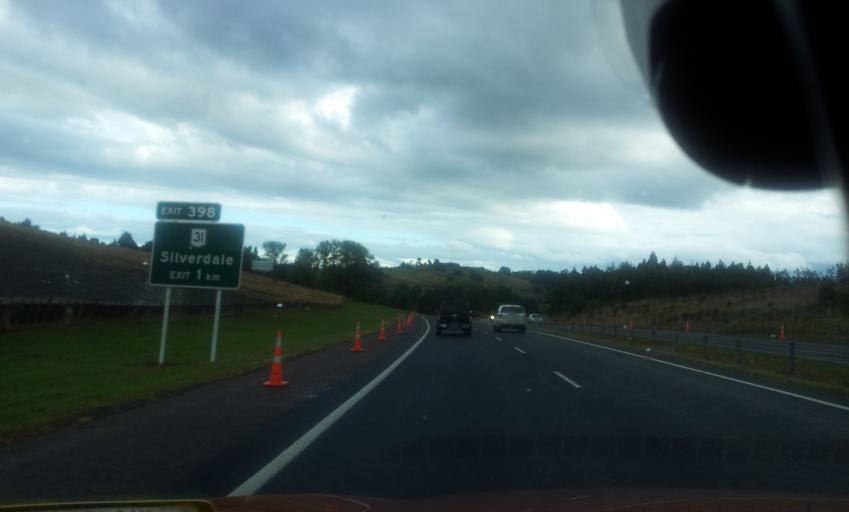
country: NZ
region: Auckland
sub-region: Auckland
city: Rothesay Bay
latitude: -36.6134
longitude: 174.6609
